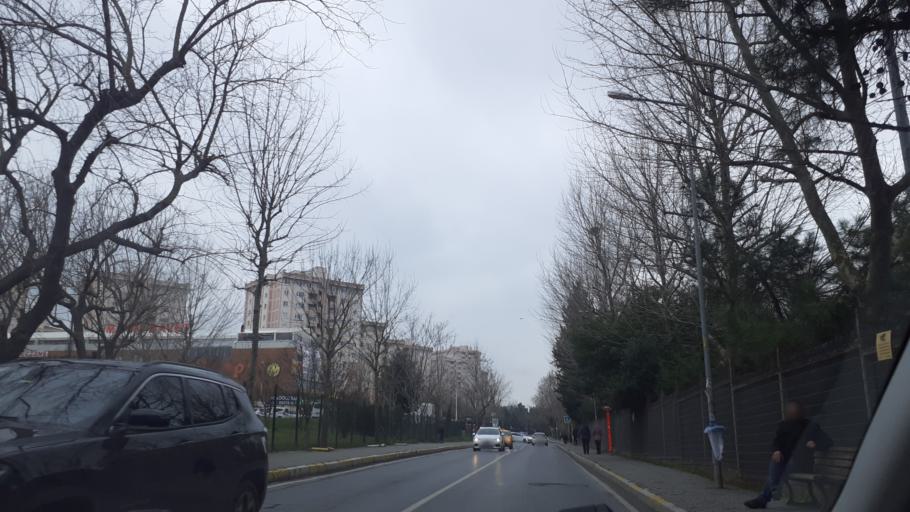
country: TR
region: Istanbul
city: Mahmutbey
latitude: 41.0494
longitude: 28.7851
